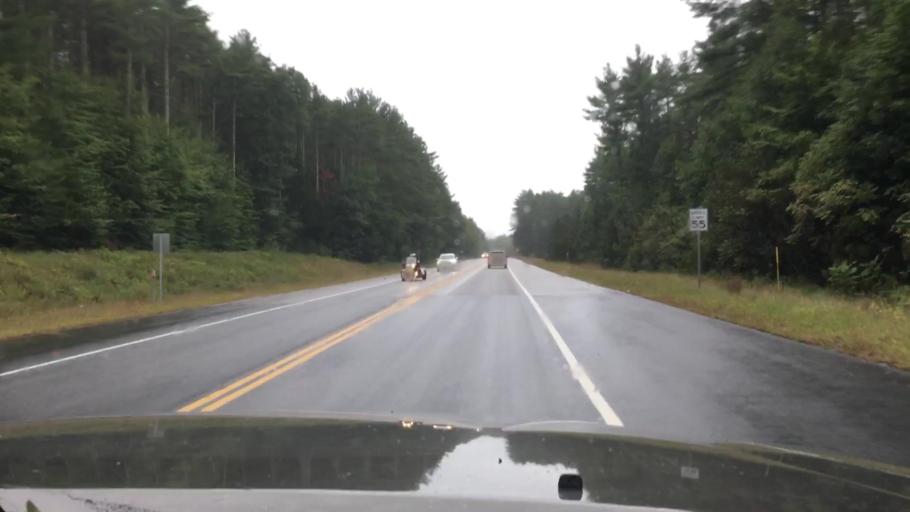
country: US
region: New Hampshire
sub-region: Cheshire County
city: Keene
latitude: 42.9265
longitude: -72.3162
